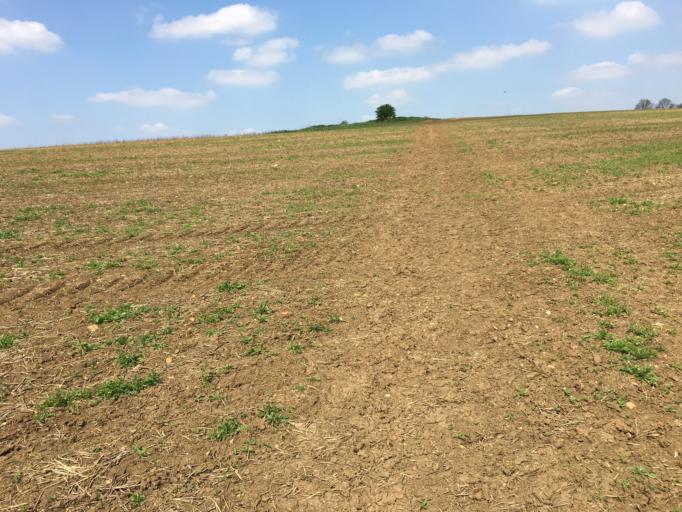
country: GB
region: England
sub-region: Leicestershire
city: Houghton on the Hill
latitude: 52.6132
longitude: -0.9955
